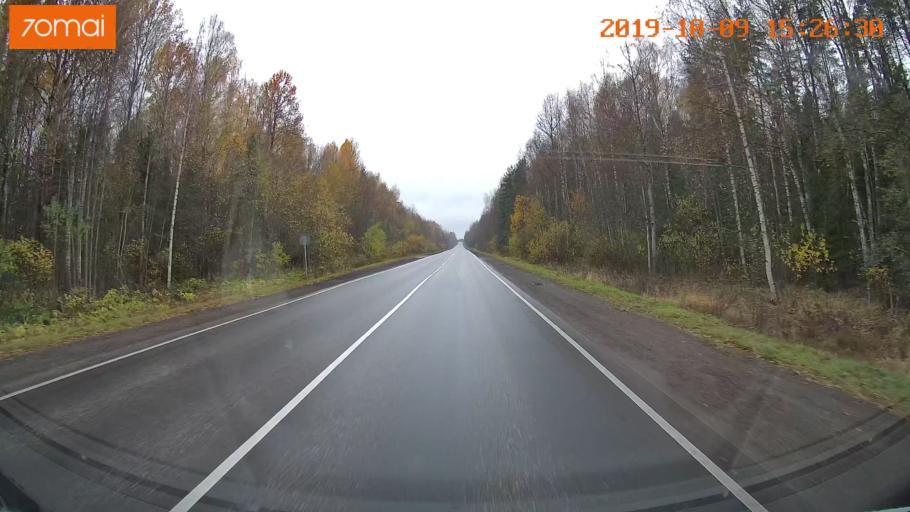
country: RU
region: Kostroma
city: Susanino
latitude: 58.0196
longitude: 41.4023
